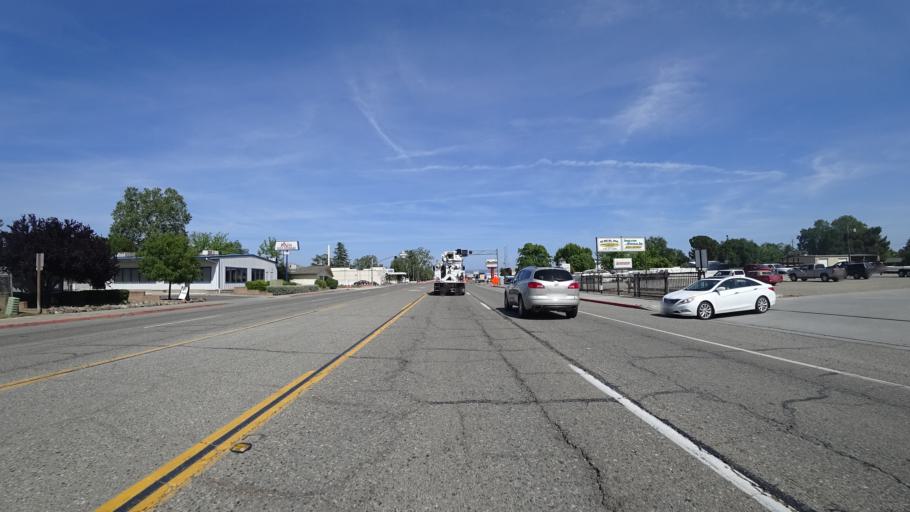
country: US
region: California
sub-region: Tehama County
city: Red Bluff
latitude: 40.1860
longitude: -122.2072
